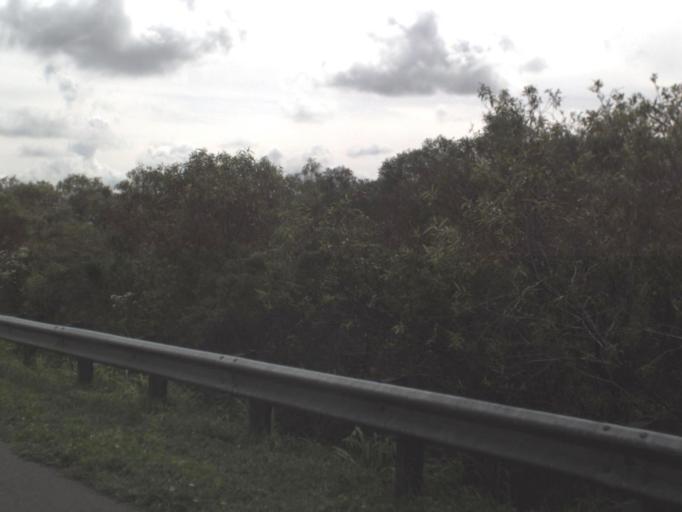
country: US
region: Florida
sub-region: Highlands County
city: Lake Placid
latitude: 27.2092
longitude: -81.1952
